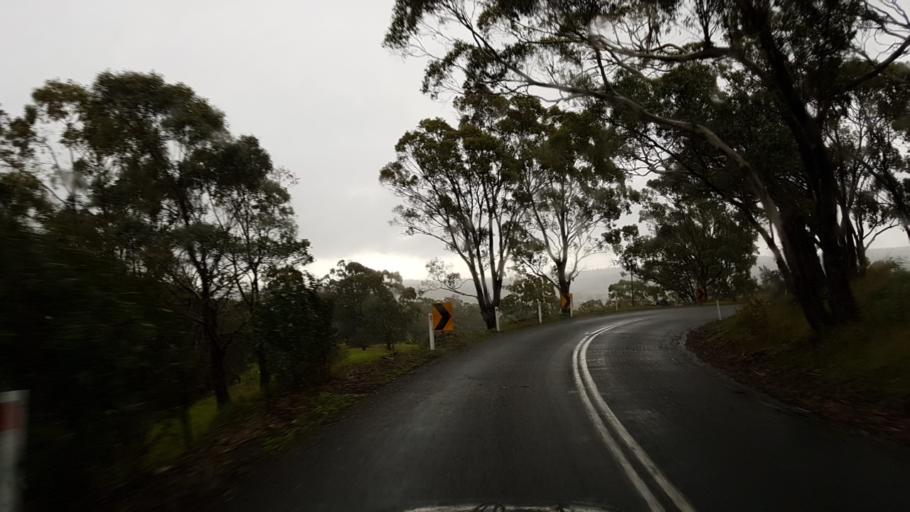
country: AU
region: South Australia
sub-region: Onkaparinga
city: Craigburn Farm
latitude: -35.0663
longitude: 138.6223
